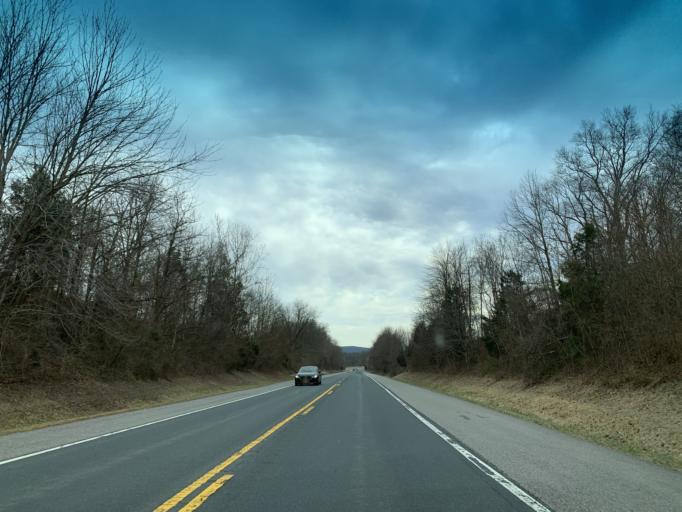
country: US
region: Maryland
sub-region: Washington County
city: Keedysville
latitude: 39.4396
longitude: -77.6634
